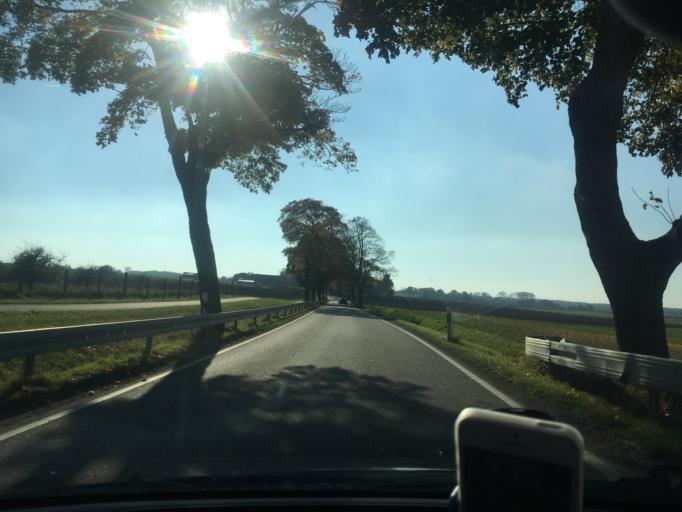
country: DE
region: Mecklenburg-Vorpommern
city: Stralendorf
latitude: 53.5704
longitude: 11.2820
